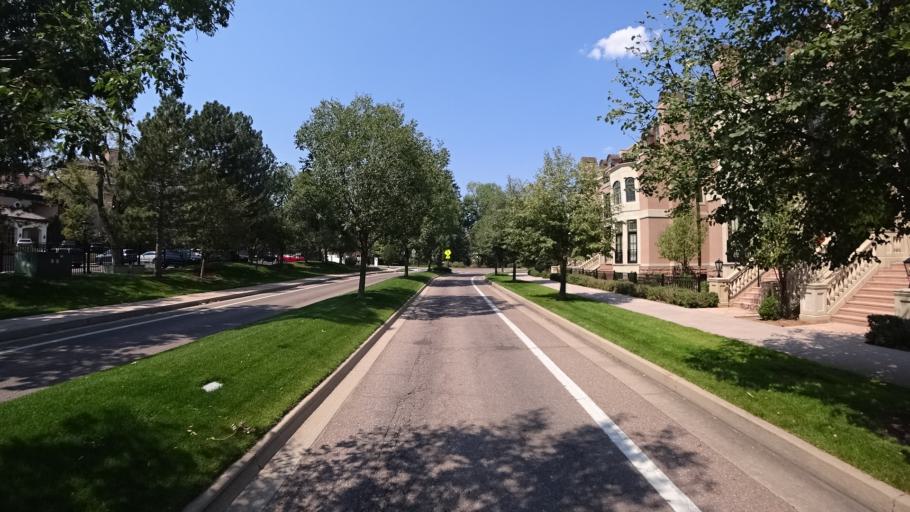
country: US
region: Colorado
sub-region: El Paso County
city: Colorado Springs
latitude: 38.7898
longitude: -104.8484
